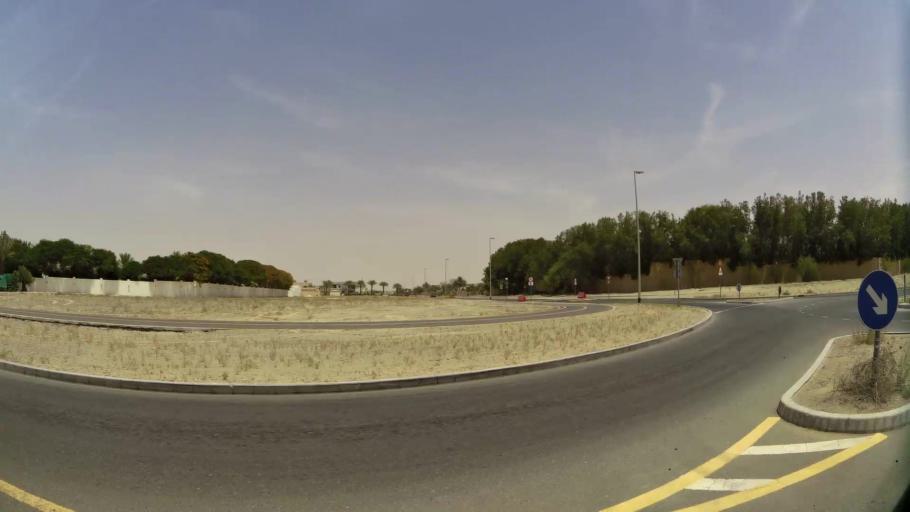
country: AE
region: Ash Shariqah
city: Sharjah
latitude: 25.2440
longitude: 55.4783
